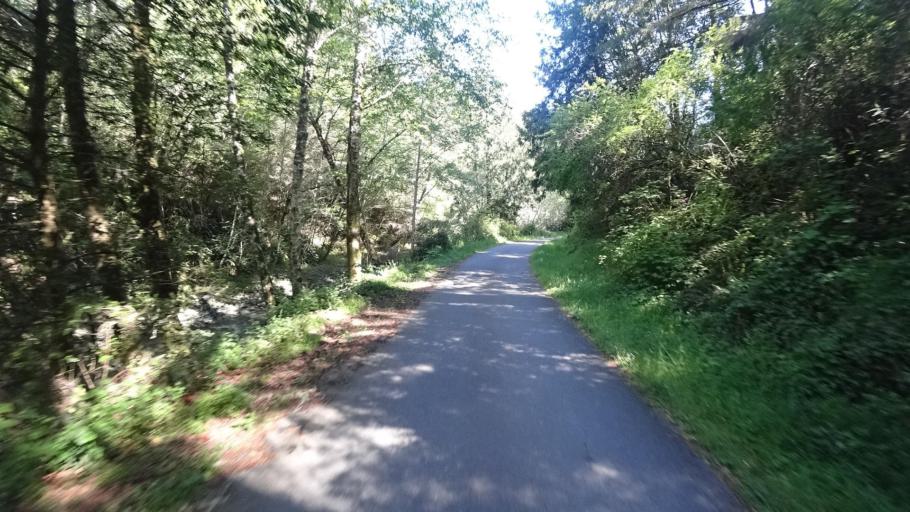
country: US
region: California
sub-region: Humboldt County
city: Ferndale
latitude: 40.5093
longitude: -124.2004
